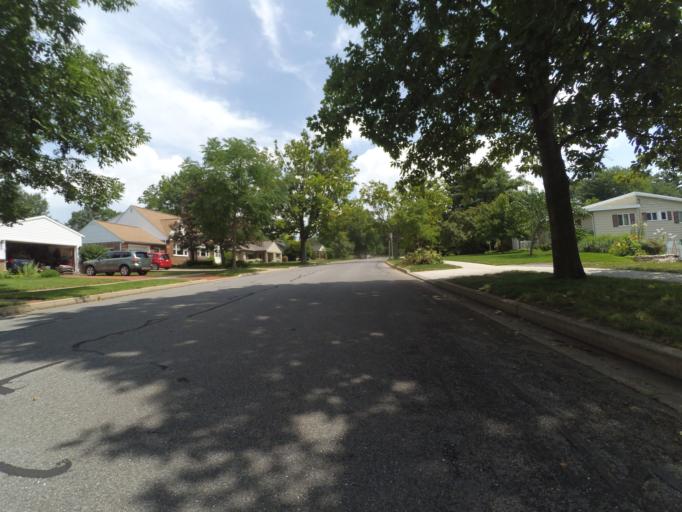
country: US
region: Pennsylvania
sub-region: Centre County
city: State College
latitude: 40.7875
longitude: -77.8453
